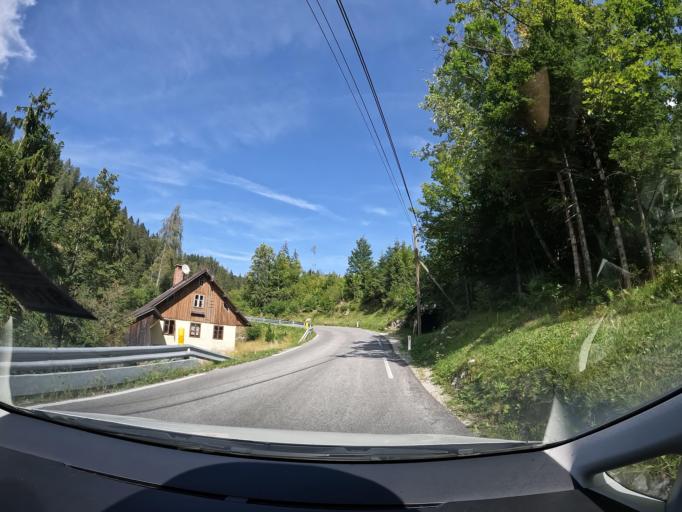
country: AT
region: Carinthia
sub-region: Politischer Bezirk Klagenfurt Land
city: Schiefling am See
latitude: 46.5902
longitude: 14.0678
